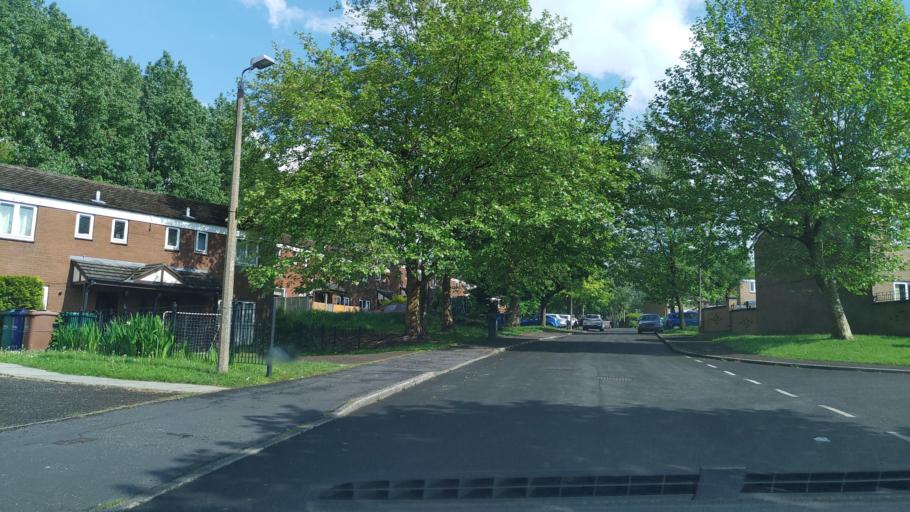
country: GB
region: England
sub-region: Lancashire
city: Clayton-le-Woods
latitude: 53.7155
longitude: -2.6359
